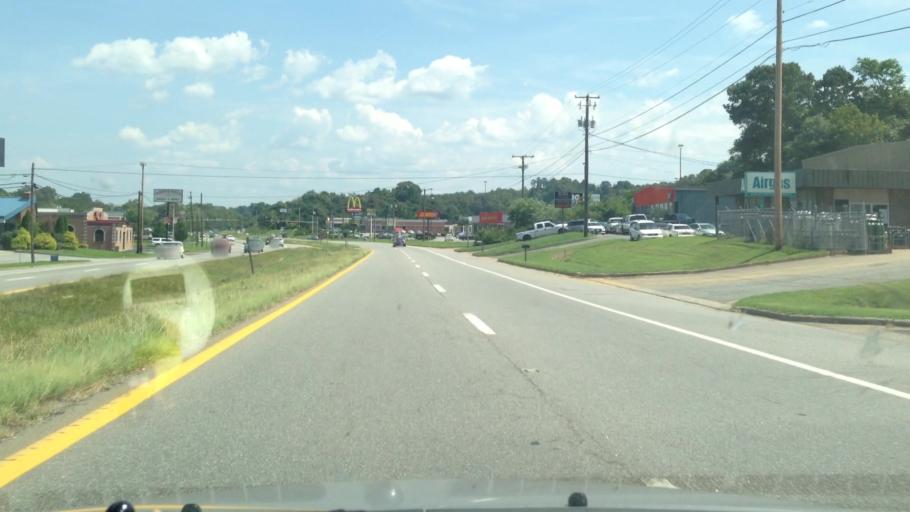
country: US
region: Virginia
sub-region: City of Martinsville
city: Martinsville
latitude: 36.6554
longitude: -79.8772
